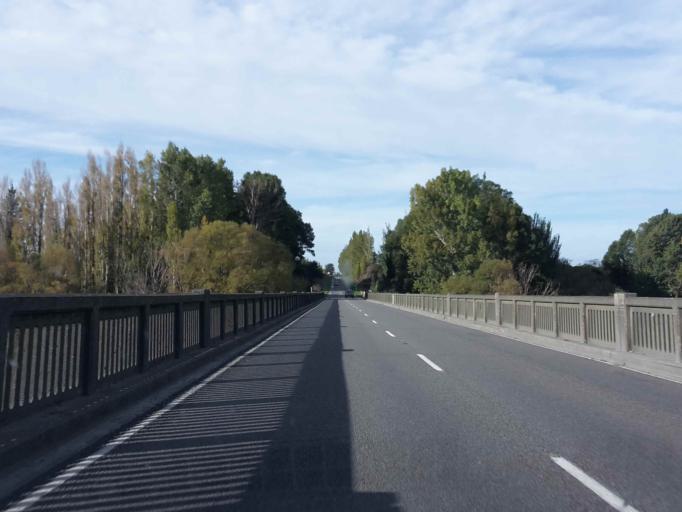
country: NZ
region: Canterbury
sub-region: Ashburton District
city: Tinwald
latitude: -44.0505
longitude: 171.4072
